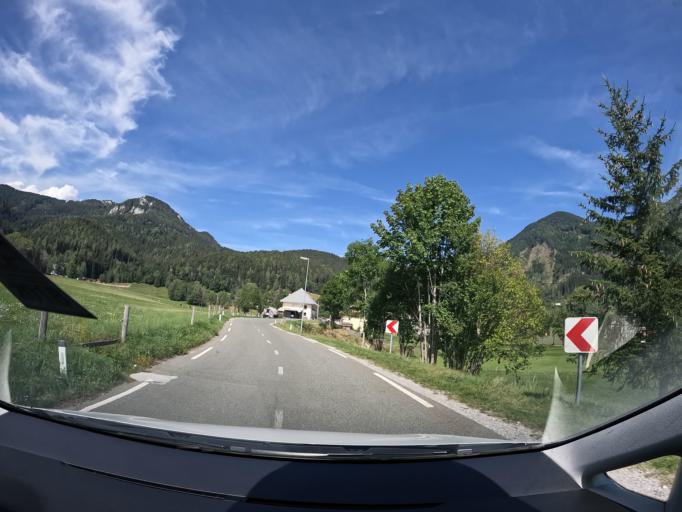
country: AT
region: Carinthia
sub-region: Politischer Bezirk Feldkirchen
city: Feldkirchen in Karnten
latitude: 46.7336
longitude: 14.1462
